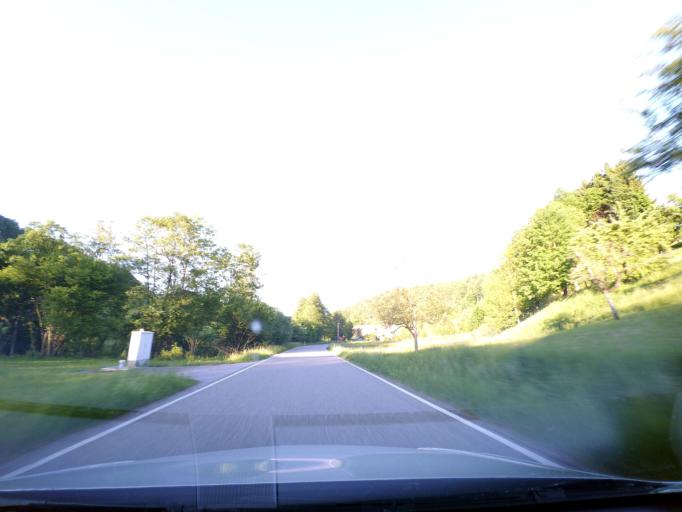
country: DE
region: Baden-Wuerttemberg
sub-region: Regierungsbezirk Stuttgart
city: Kaisersbach
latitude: 48.9581
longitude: 9.6132
